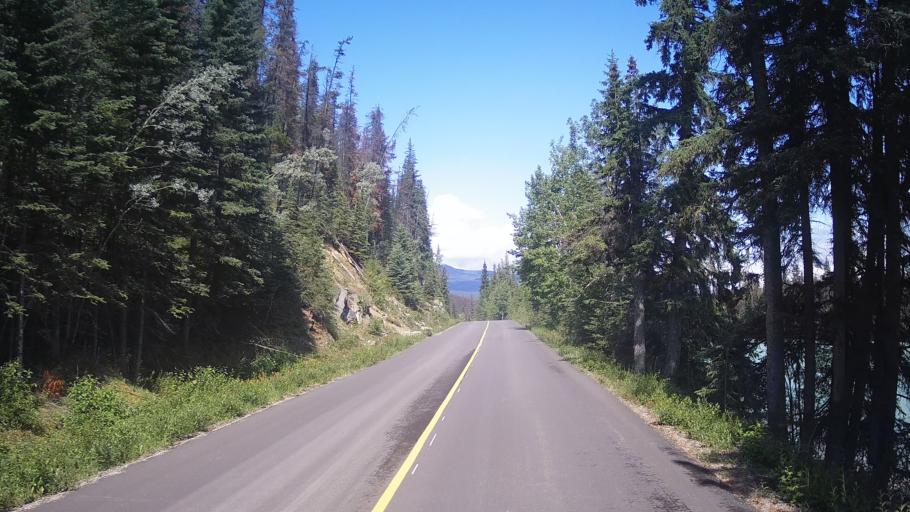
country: CA
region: Alberta
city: Jasper Park Lodge
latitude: 52.7393
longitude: -117.9597
